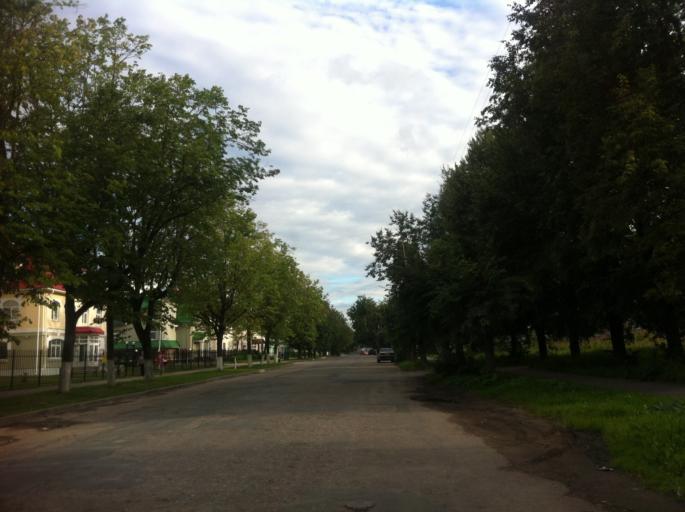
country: RU
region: Pskov
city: Pskov
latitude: 57.8236
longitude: 28.3195
